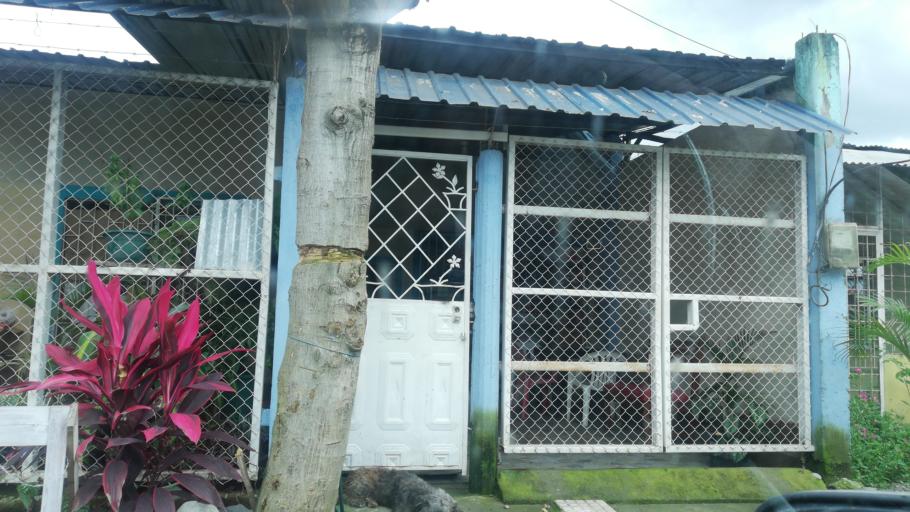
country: EC
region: Canar
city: La Troncal
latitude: -2.3282
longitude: -79.3952
